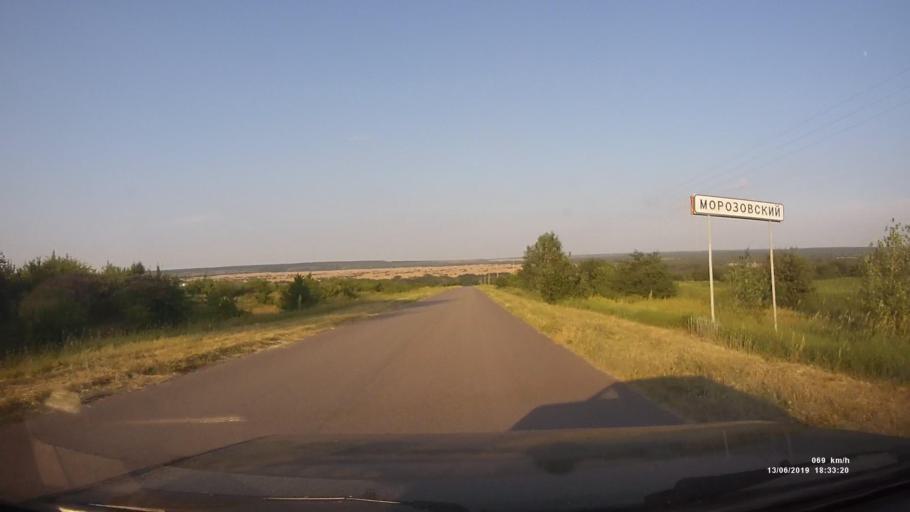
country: RU
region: Rostov
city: Kazanskaya
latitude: 49.8704
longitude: 41.3809
